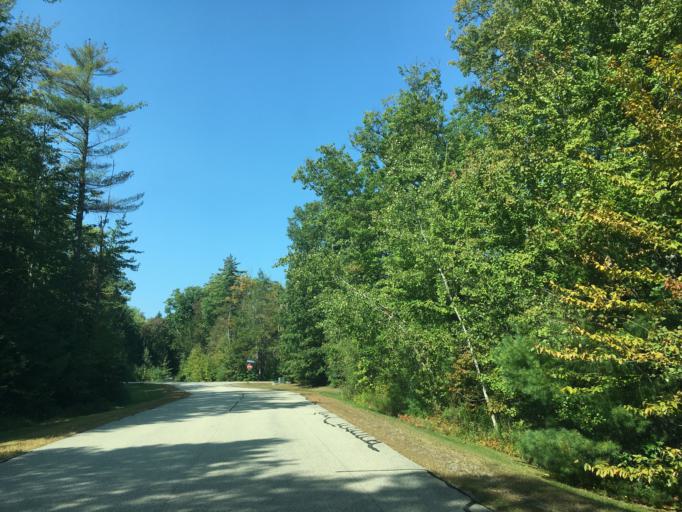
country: US
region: New Hampshire
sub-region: Rockingham County
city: Stratham Station
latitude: 43.0067
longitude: -70.8898
